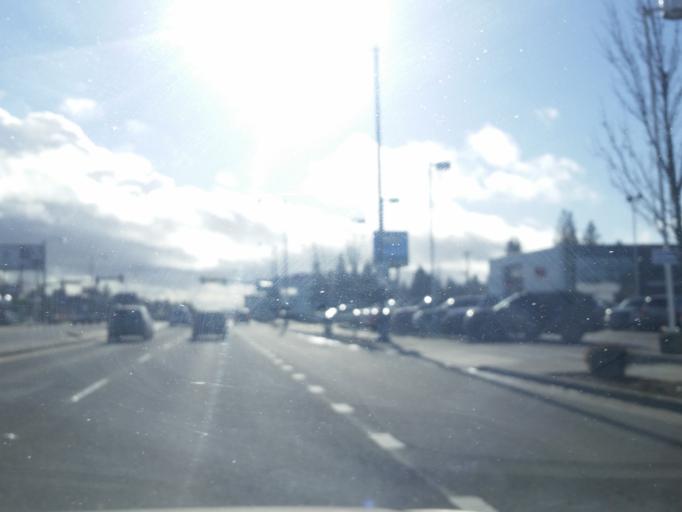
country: US
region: Washington
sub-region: King County
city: Shoreline
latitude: 47.7536
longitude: -122.3457
